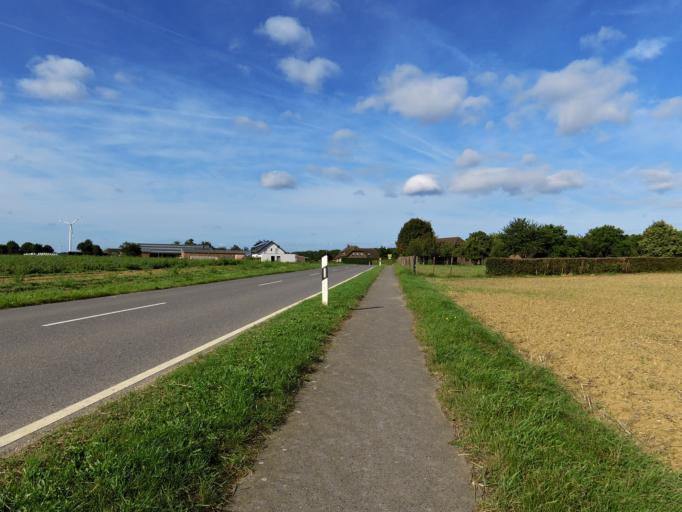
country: DE
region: North Rhine-Westphalia
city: Niedermerz
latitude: 50.8774
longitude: 6.2447
